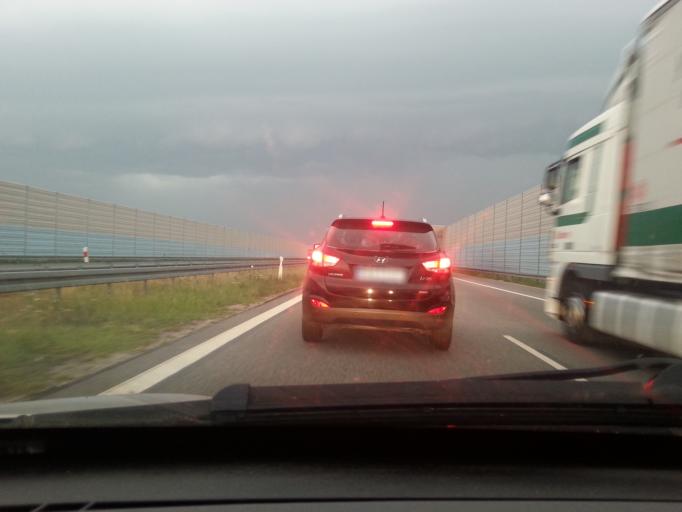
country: PL
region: Lodz Voivodeship
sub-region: powiat Lowicki
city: Lyszkowice
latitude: 51.9952
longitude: 19.9170
